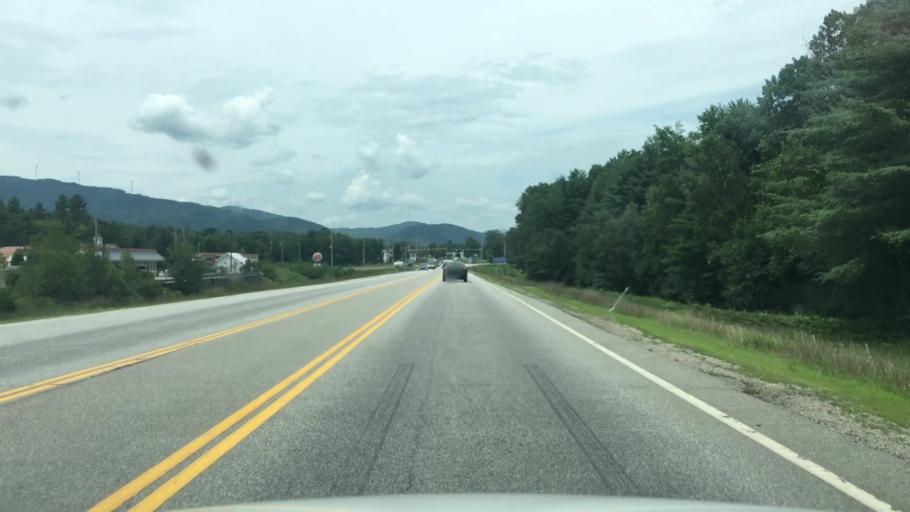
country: US
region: New Hampshire
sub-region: Grafton County
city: Plymouth
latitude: 43.7703
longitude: -71.7174
